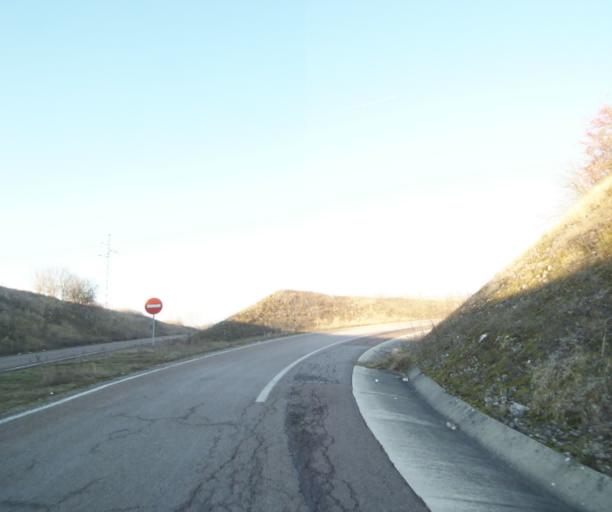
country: FR
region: Champagne-Ardenne
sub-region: Departement de la Haute-Marne
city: Chevillon
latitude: 48.5407
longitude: 5.0844
